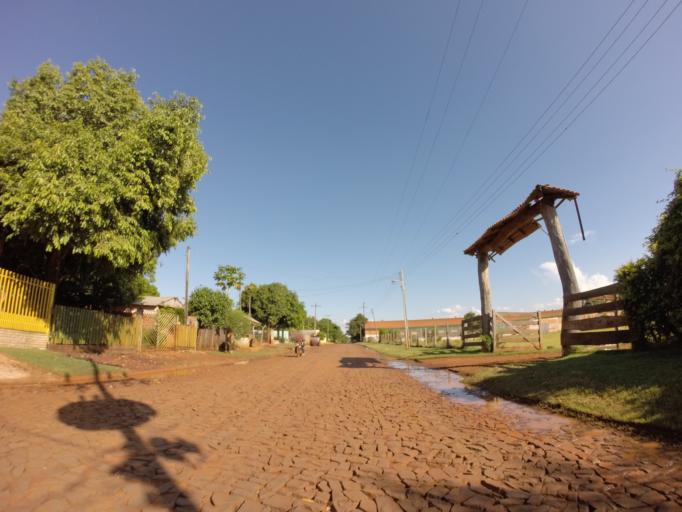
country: PY
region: Alto Parana
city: Ciudad del Este
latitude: -25.3909
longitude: -54.6498
